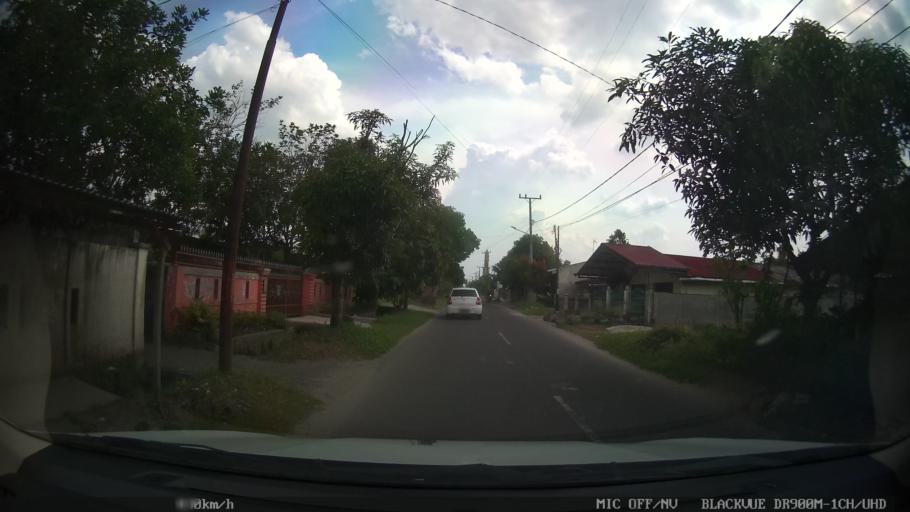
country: ID
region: North Sumatra
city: Binjai
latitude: 3.6297
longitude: 98.5020
